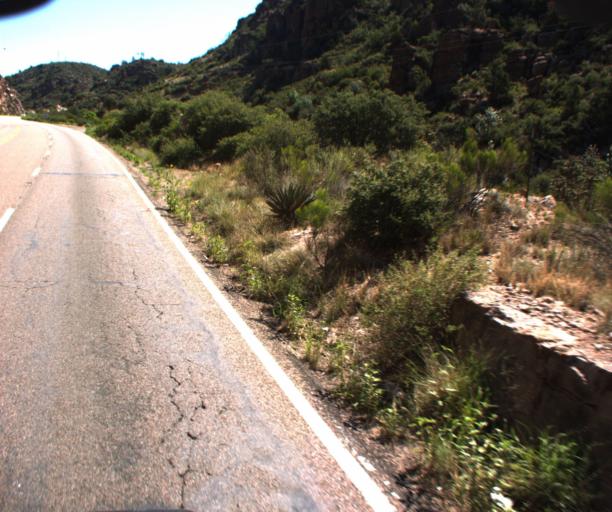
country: US
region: Arizona
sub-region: Pinal County
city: Superior
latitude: 33.3330
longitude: -111.0292
